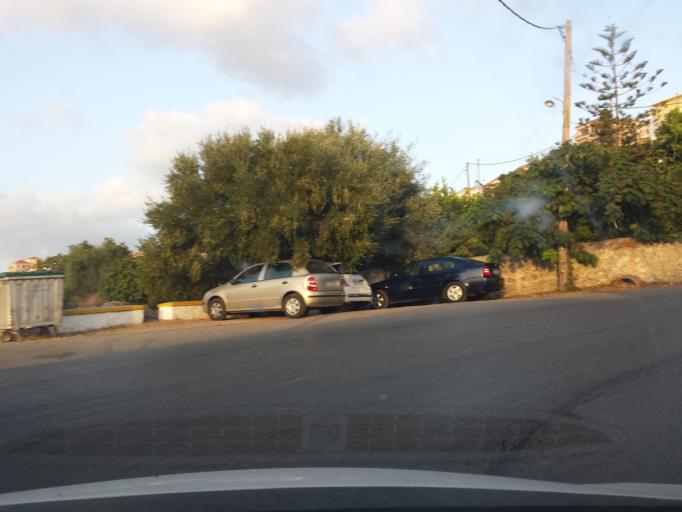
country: GR
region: Peloponnese
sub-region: Nomos Messinias
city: Pylos
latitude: 36.9161
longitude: 21.6987
